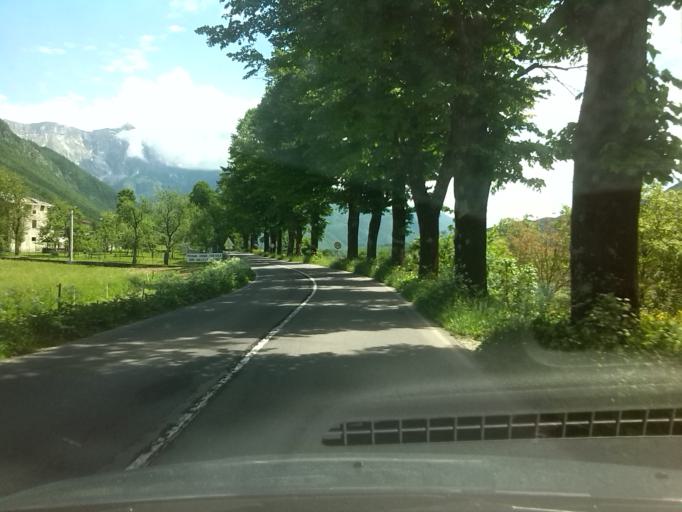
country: SI
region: Kobarid
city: Kobarid
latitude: 46.2456
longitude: 13.5258
